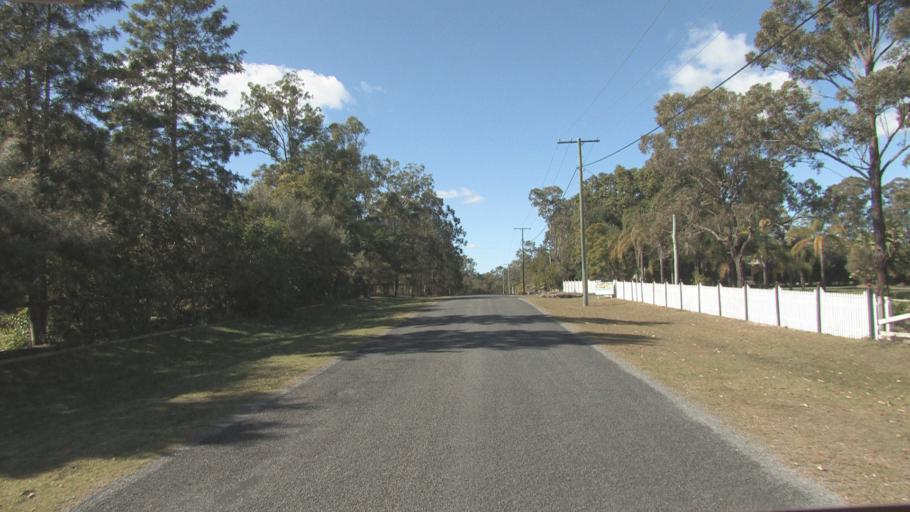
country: AU
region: Queensland
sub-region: Logan
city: Chambers Flat
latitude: -27.7471
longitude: 153.0976
